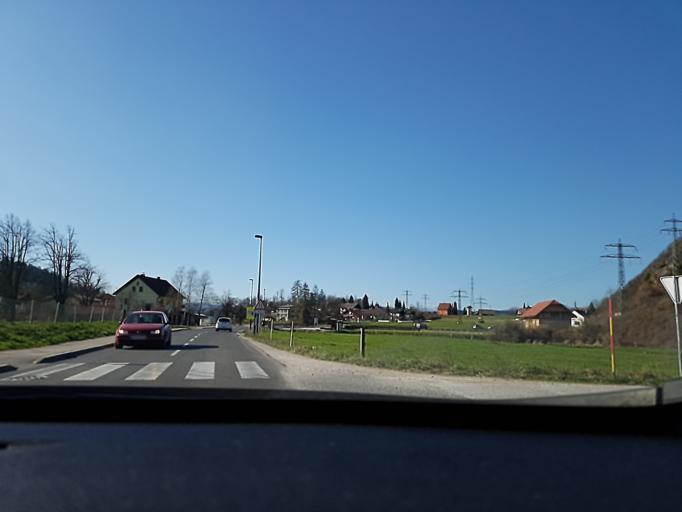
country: SI
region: Medvode
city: Zgornje Pirnice
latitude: 46.1219
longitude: 14.4468
